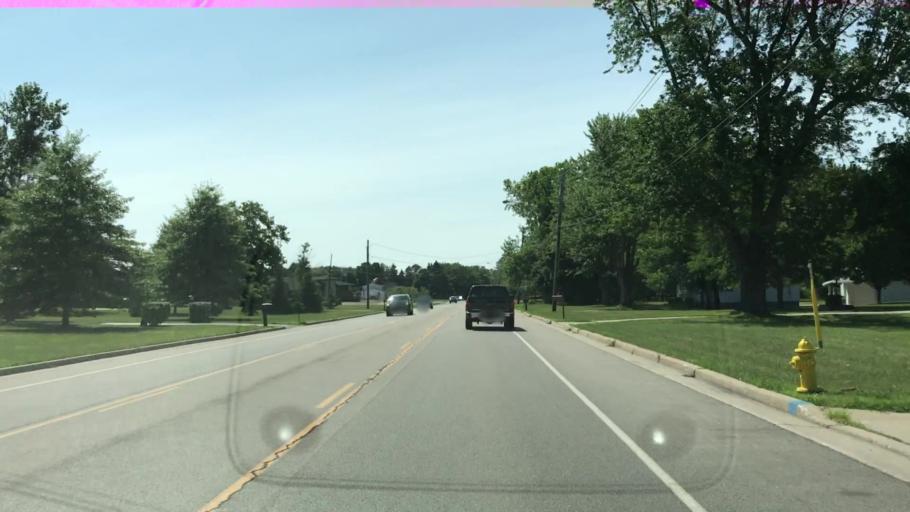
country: US
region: New York
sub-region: Erie County
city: Depew
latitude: 42.8802
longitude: -78.7165
